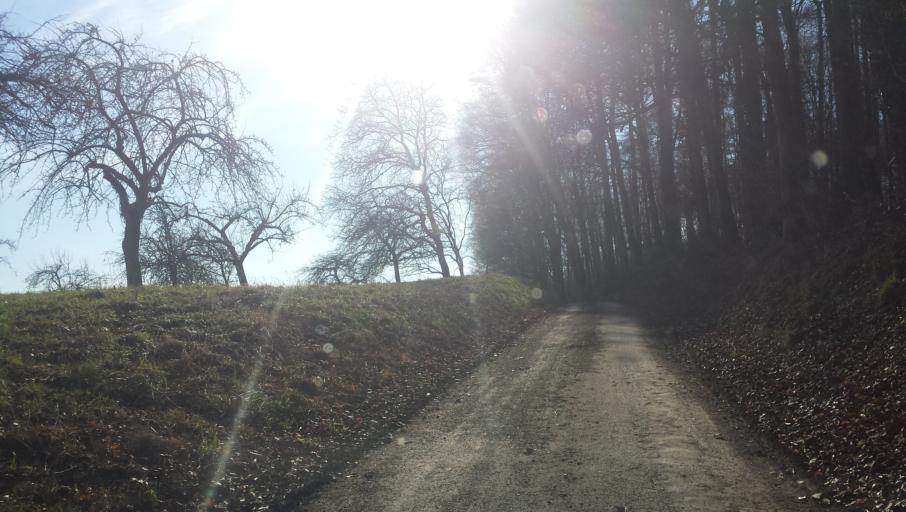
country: DE
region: Baden-Wuerttemberg
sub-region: Karlsruhe Region
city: Meckesheim
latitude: 49.3451
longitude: 8.8351
